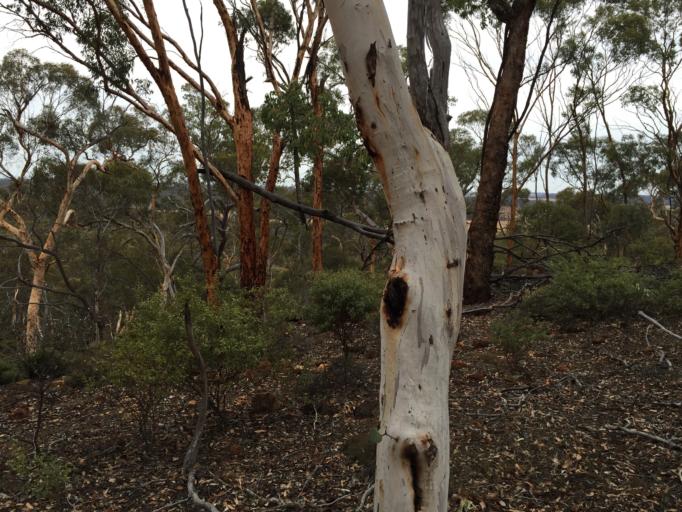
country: AU
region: Western Australia
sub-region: Narrogin
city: Narrogin
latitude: -32.7984
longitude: 116.9420
